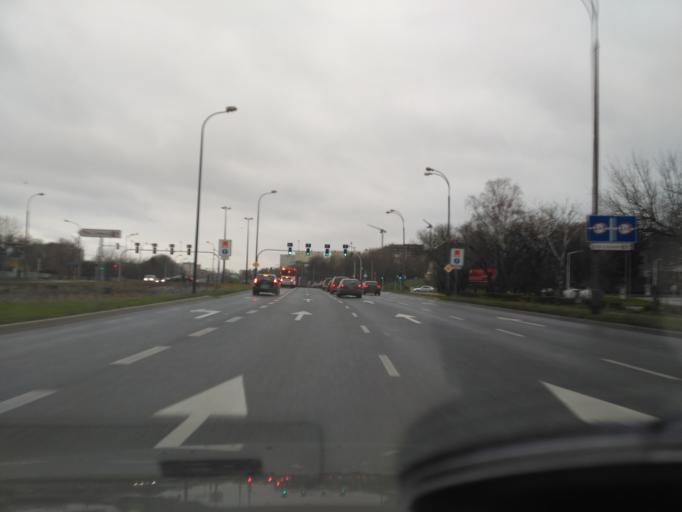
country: PL
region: Lublin Voivodeship
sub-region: Powiat lubelski
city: Lublin
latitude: 51.2531
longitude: 22.5627
